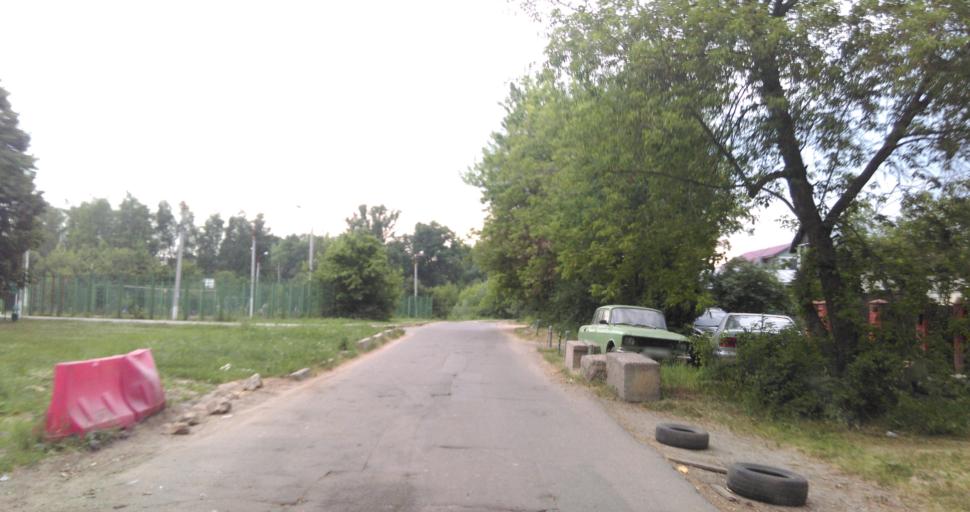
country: RU
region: Moskovskaya
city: Vostryakovo
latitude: 55.3979
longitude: 37.8184
